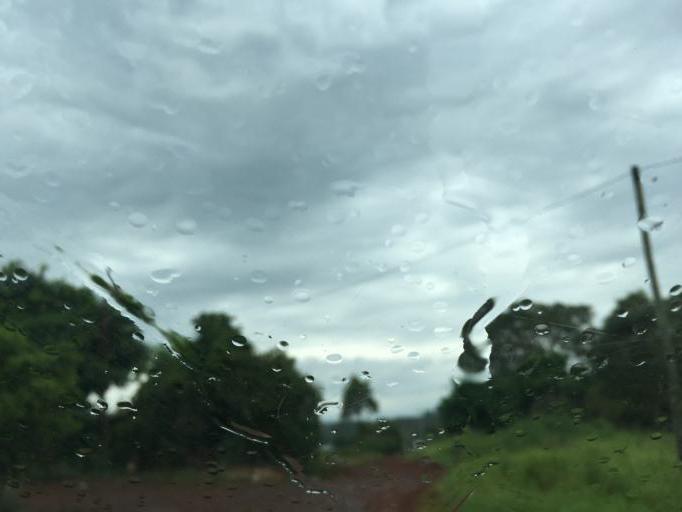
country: PY
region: Alto Parana
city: Ciudad del Este
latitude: -25.4388
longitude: -54.6538
